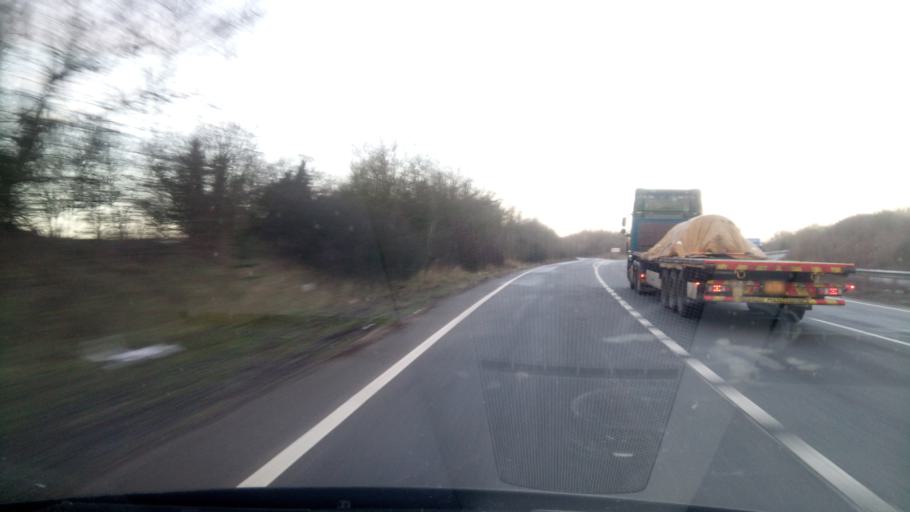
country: GB
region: England
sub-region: Peterborough
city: Castor
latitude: 52.5717
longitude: -0.3204
